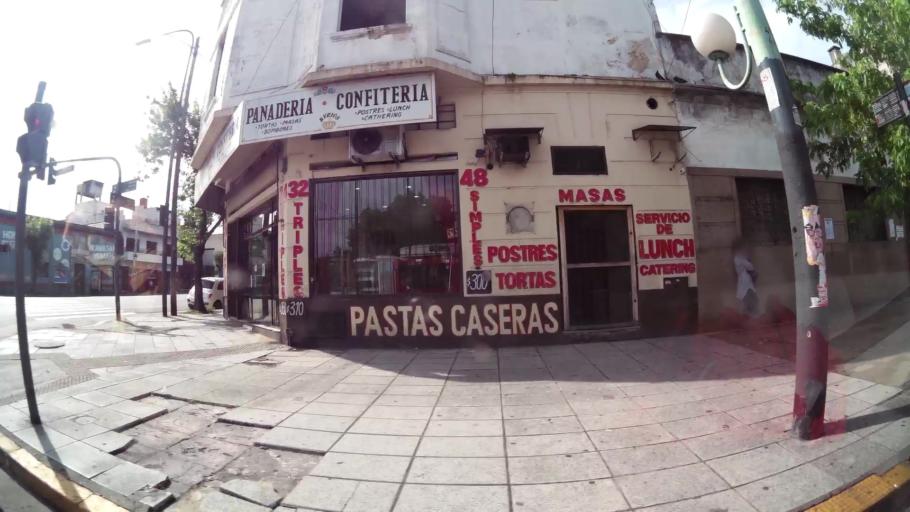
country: AR
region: Buenos Aires F.D.
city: Buenos Aires
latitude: -34.6401
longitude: -58.4233
